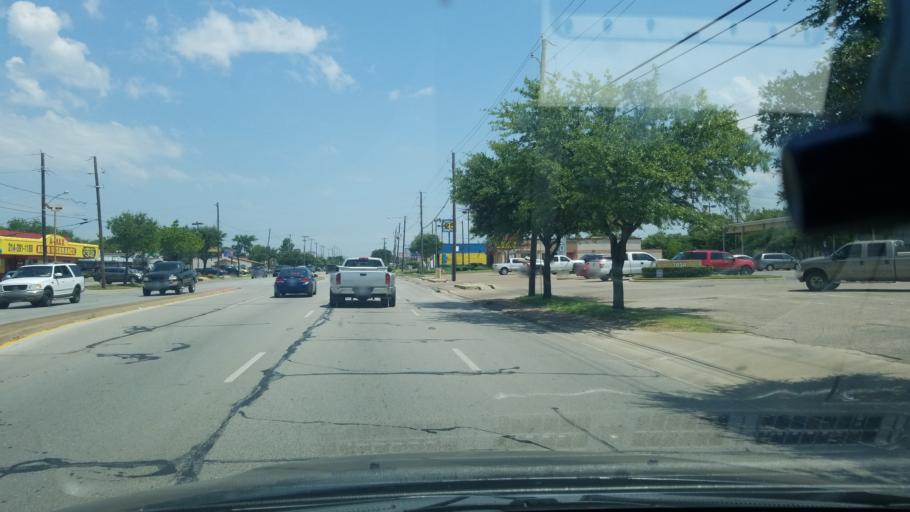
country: US
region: Texas
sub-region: Dallas County
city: Balch Springs
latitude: 32.7434
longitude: -96.6828
